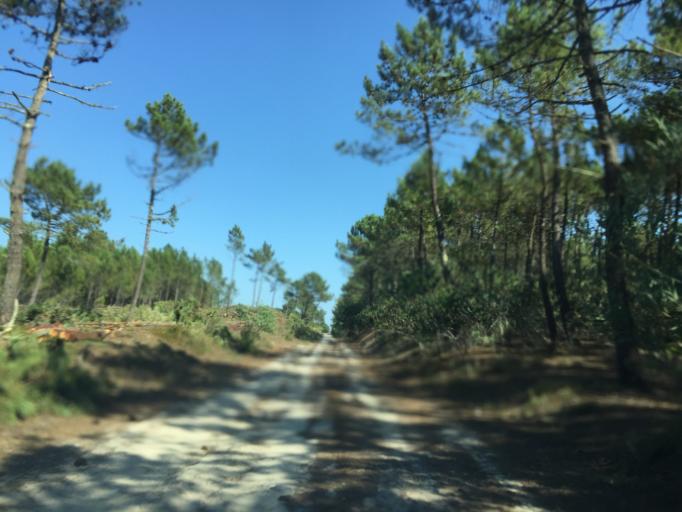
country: PT
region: Coimbra
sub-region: Figueira da Foz
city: Tavarede
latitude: 40.2618
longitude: -8.8566
